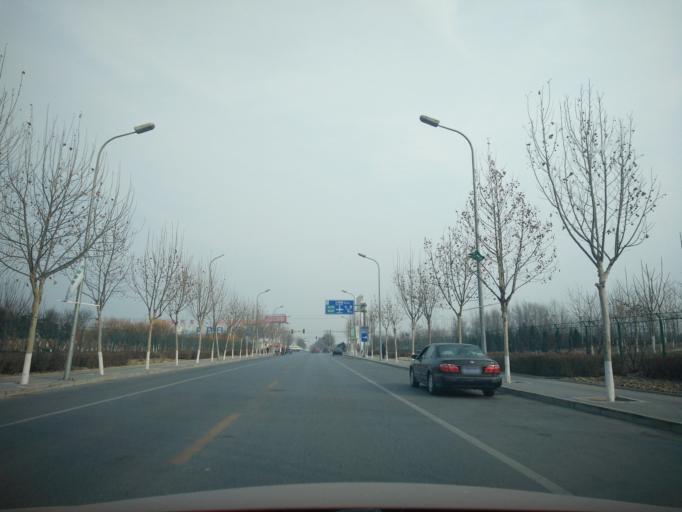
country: CN
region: Beijing
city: Yinghai
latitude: 39.7150
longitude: 116.4003
